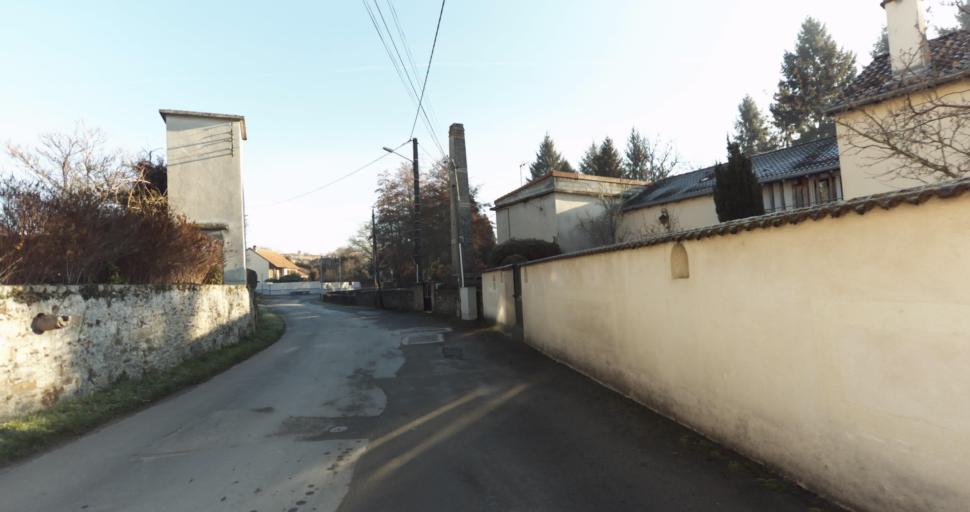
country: FR
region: Limousin
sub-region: Departement de la Haute-Vienne
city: Aixe-sur-Vienne
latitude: 45.7992
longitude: 1.1519
